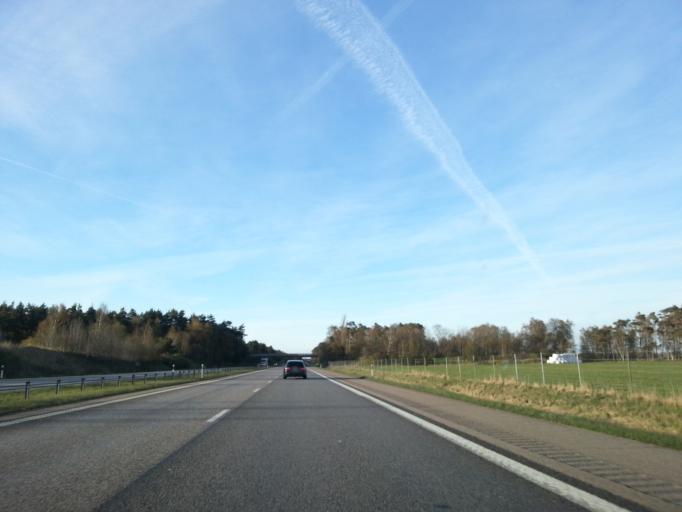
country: SE
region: Halland
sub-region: Laholms Kommun
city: Mellbystrand
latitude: 56.4747
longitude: 12.9436
